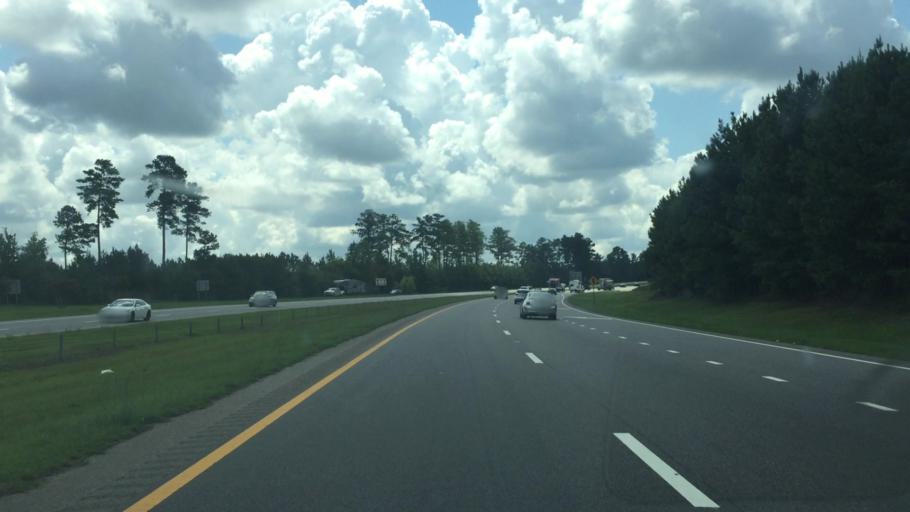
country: US
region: North Carolina
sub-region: Richmond County
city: East Rockingham
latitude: 34.9100
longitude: -79.7915
